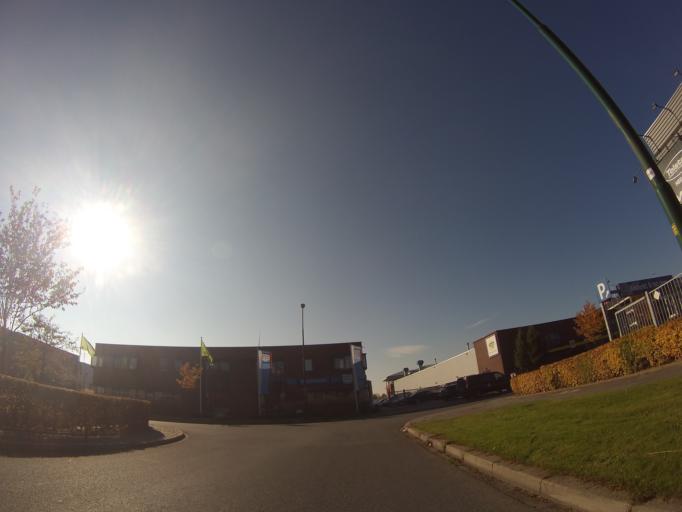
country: NL
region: Utrecht
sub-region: Gemeente Houten
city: Houten
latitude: 52.0234
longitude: 5.1463
